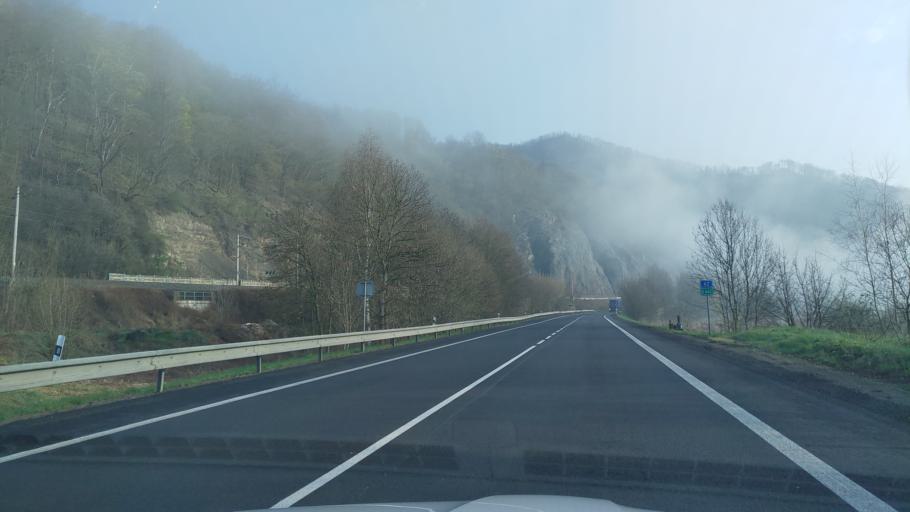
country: CZ
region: Ustecky
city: Povrly
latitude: 50.6774
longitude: 14.1659
